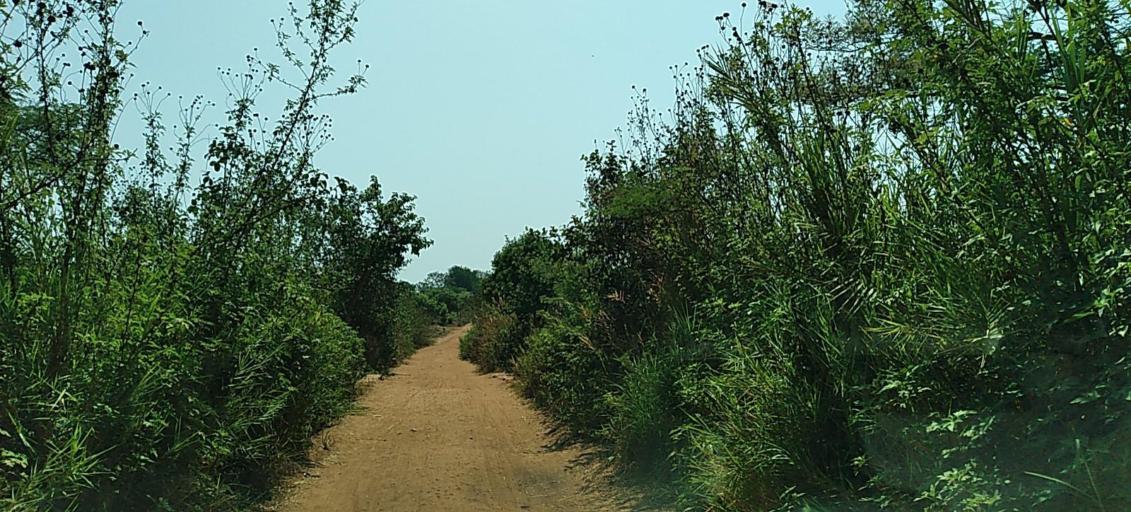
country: ZM
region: Copperbelt
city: Luanshya
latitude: -13.3486
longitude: 28.3955
